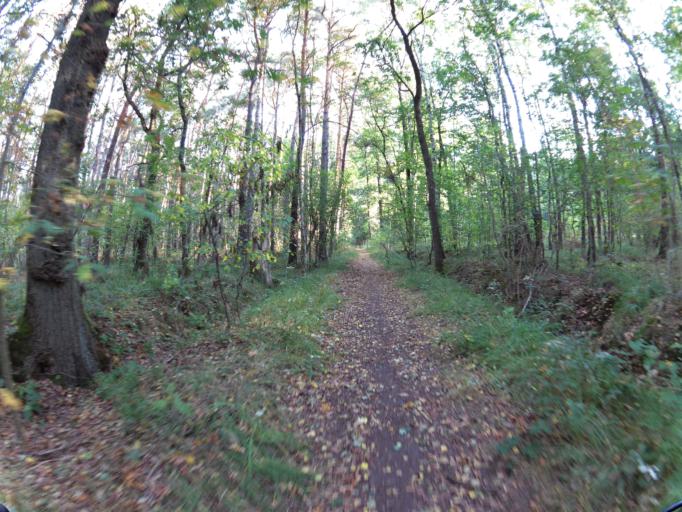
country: DE
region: North Rhine-Westphalia
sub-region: Regierungsbezirk Koln
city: Gangelt
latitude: 50.9715
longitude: 6.0132
